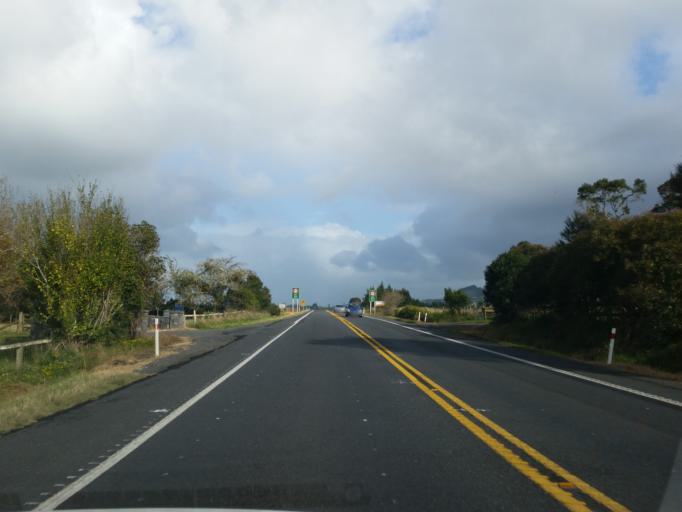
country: NZ
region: Auckland
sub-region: Auckland
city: Pukekohe East
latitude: -37.2133
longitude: 175.0719
